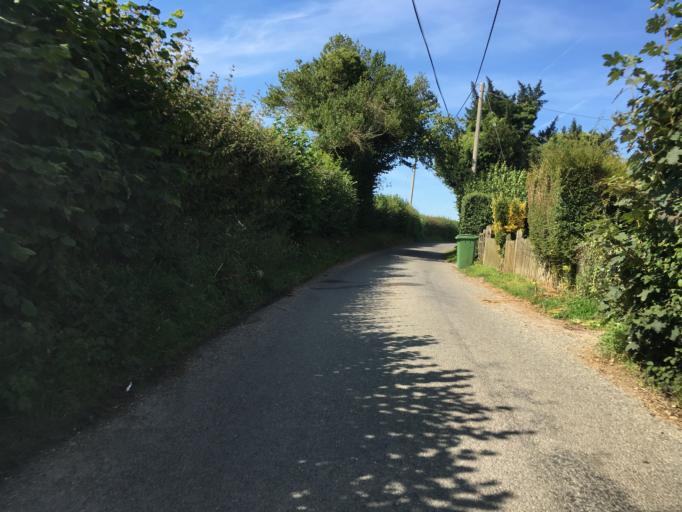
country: GB
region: England
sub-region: Hampshire
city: Highclere
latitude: 51.2917
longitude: -1.3741
